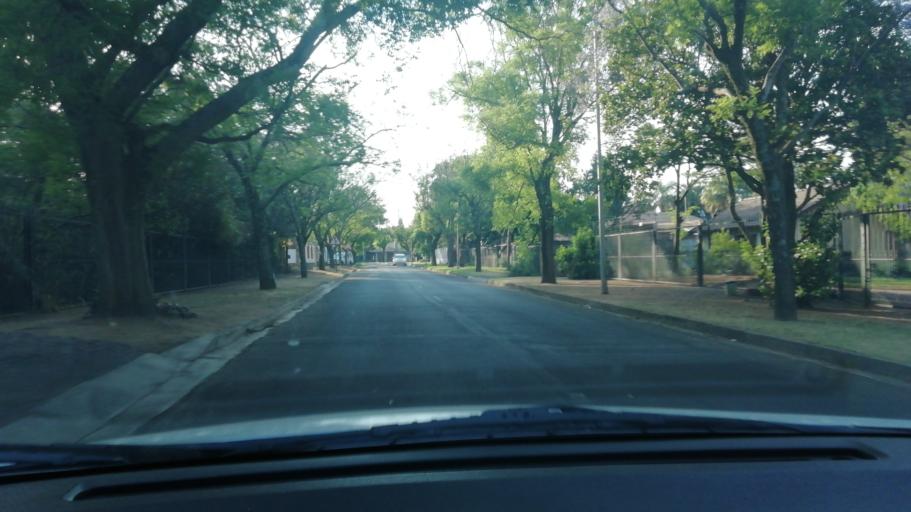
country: ZA
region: Gauteng
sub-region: Ekurhuleni Metropolitan Municipality
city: Benoni
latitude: -26.1814
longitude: 28.2893
